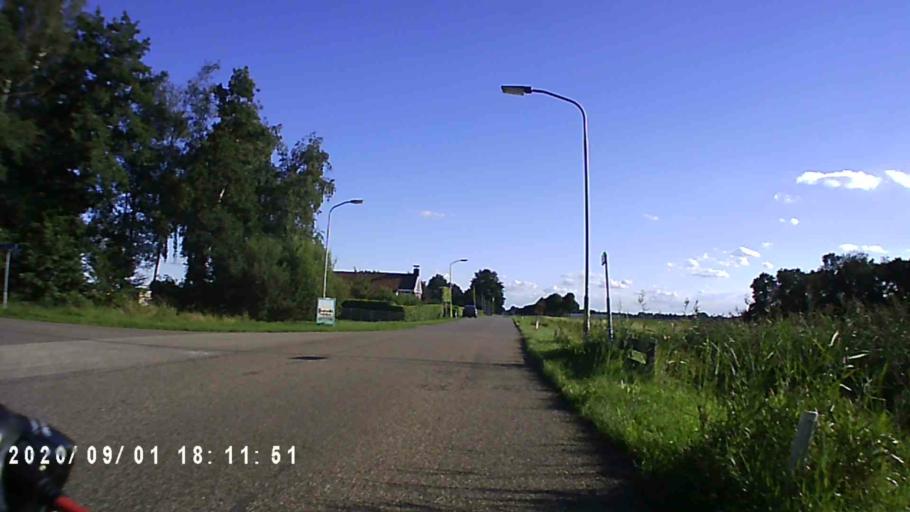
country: NL
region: Groningen
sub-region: Gemeente Hoogezand-Sappemeer
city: Sappemeer
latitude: 53.1888
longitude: 6.7851
